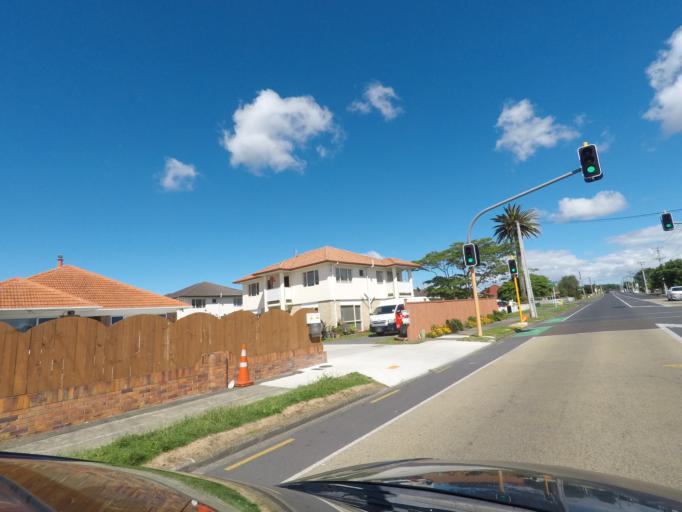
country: NZ
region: Auckland
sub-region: Auckland
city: Manukau City
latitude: -36.9777
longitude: 174.8708
